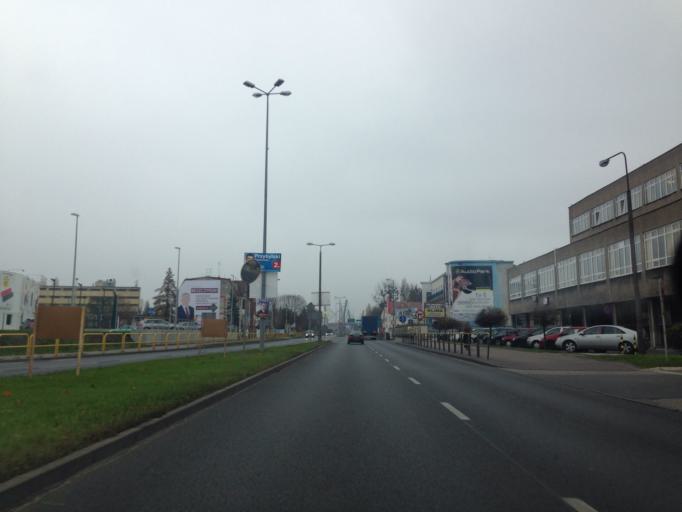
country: PL
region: Kujawsko-Pomorskie
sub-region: Torun
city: Torun
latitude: 53.0233
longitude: 18.6389
